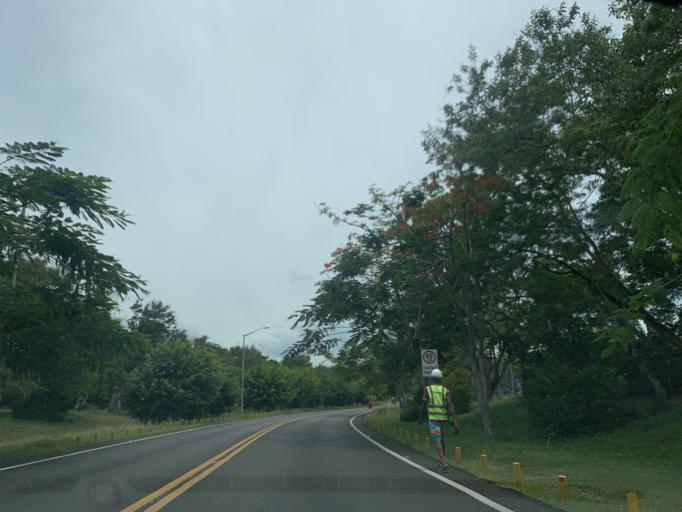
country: DO
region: Puerto Plata
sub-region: Puerto Plata
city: Puerto Plata
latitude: 19.7534
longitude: -70.5614
